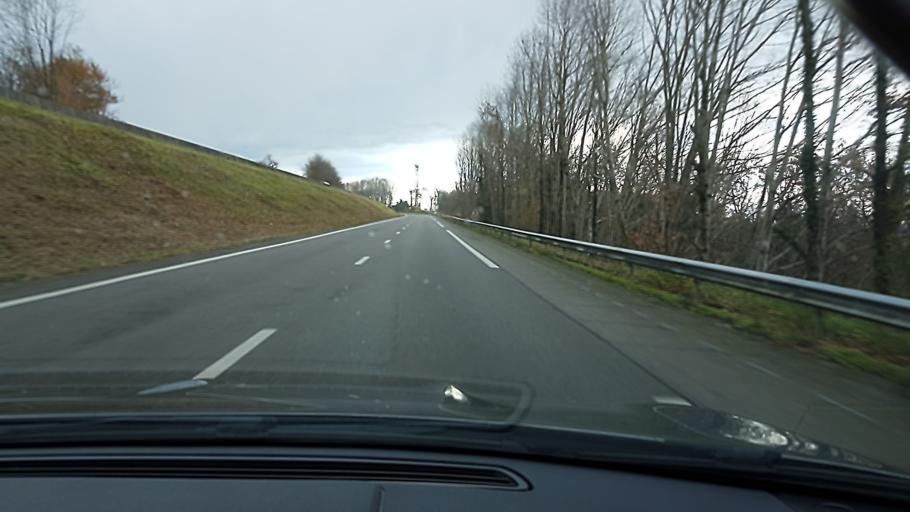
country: FR
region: Aquitaine
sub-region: Departement des Pyrenees-Atlantiques
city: Soumoulou
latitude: 43.2647
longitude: -0.1756
